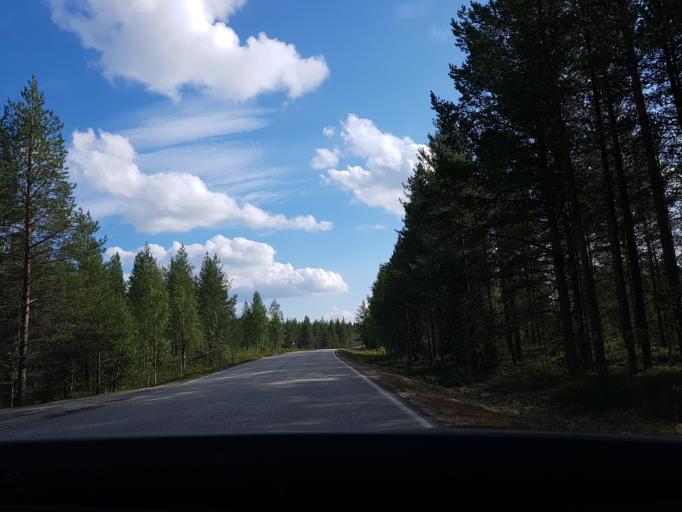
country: FI
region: Kainuu
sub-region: Kehys-Kainuu
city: Kuhmo
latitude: 64.6231
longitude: 29.6978
